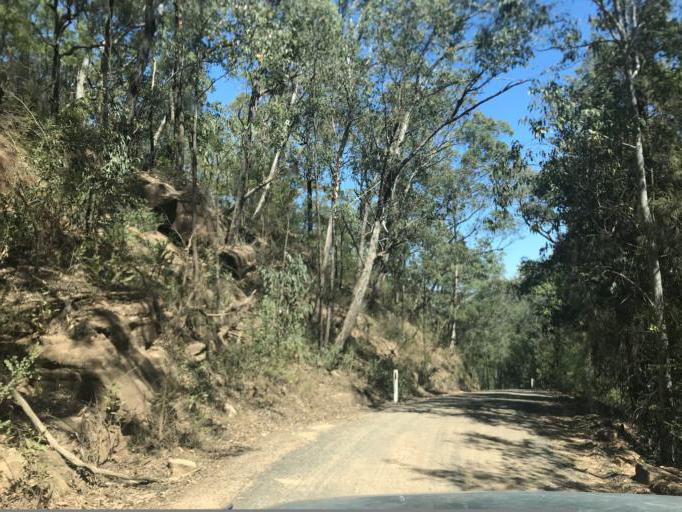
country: AU
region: New South Wales
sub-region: Wyong Shire
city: Little Jilliby
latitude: -33.1555
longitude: 151.0790
